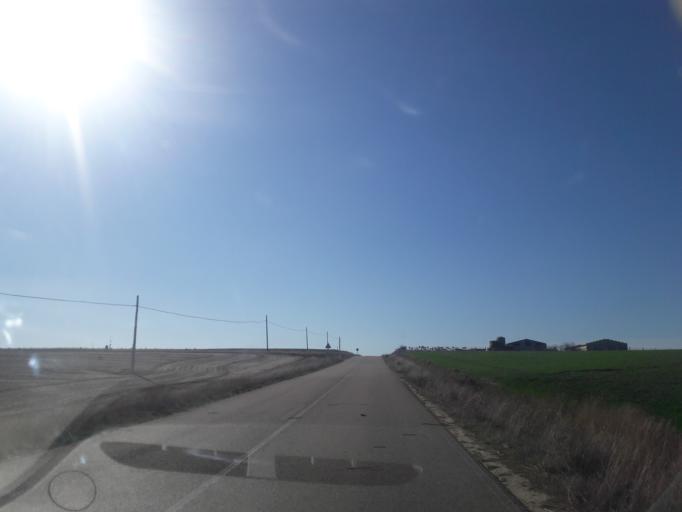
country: ES
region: Castille and Leon
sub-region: Provincia de Salamanca
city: Macotera
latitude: 40.8425
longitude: -5.3078
